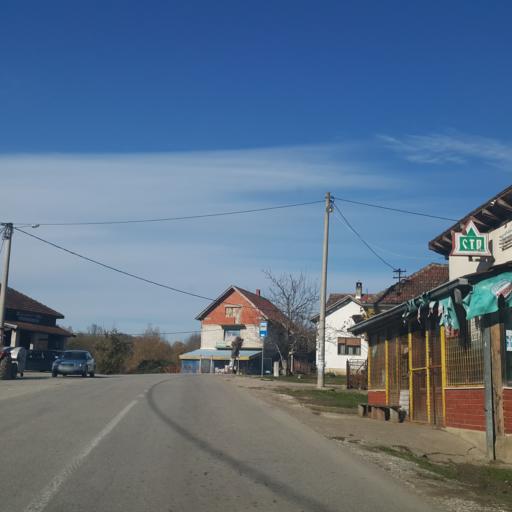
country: RS
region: Central Serbia
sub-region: Sumadijski Okrug
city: Topola
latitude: 44.2494
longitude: 20.7262
